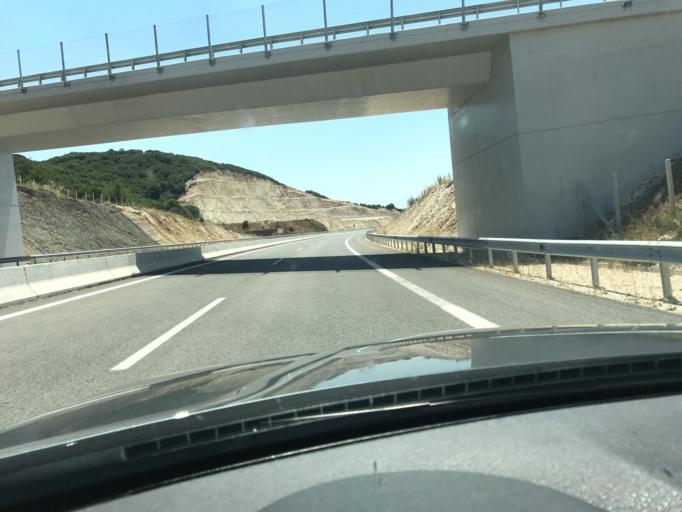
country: GR
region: Epirus
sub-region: Nomos Ioanninon
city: Agia Kyriaki
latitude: 39.4678
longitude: 20.8978
